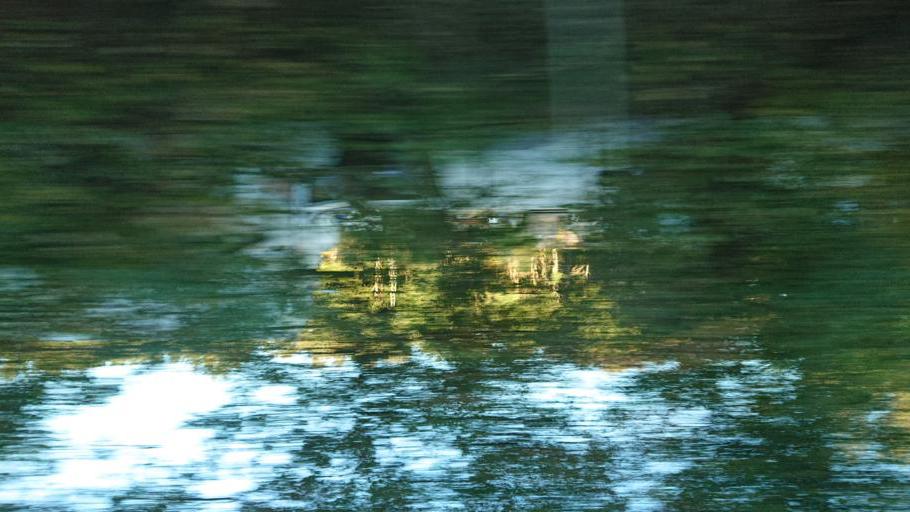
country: DE
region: Mecklenburg-Vorpommern
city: Trollenhagen
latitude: 53.6306
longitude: 13.2633
